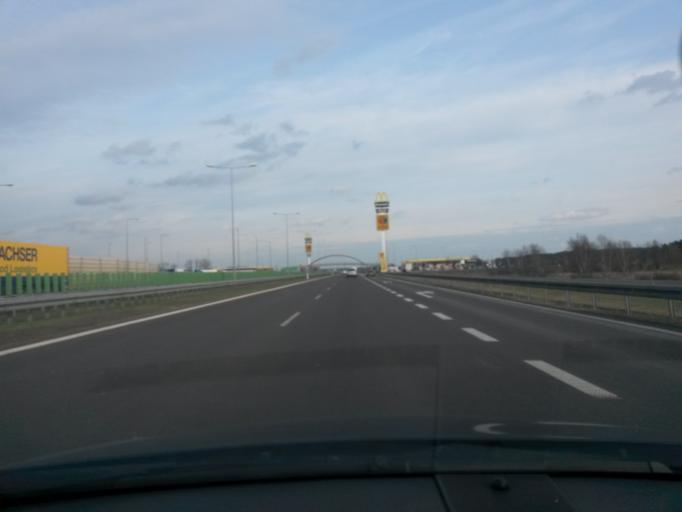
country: PL
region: Greater Poland Voivodeship
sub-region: Powiat turecki
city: Brudzew
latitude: 52.1363
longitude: 18.6295
